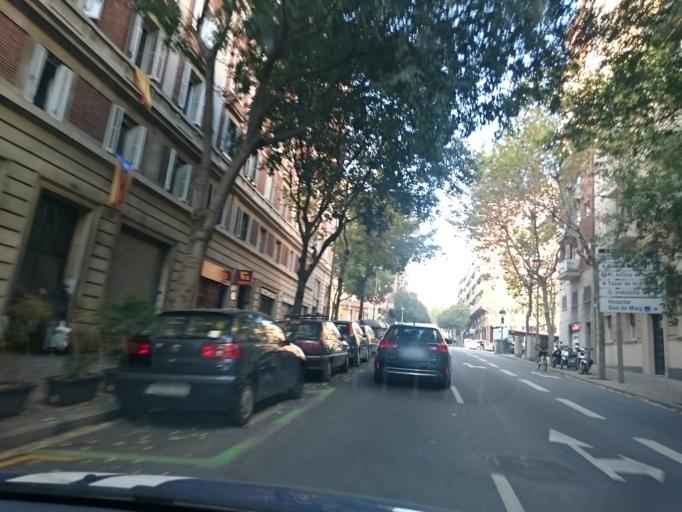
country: ES
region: Catalonia
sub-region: Provincia de Barcelona
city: Horta-Guinardo
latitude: 41.4082
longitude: 2.1739
